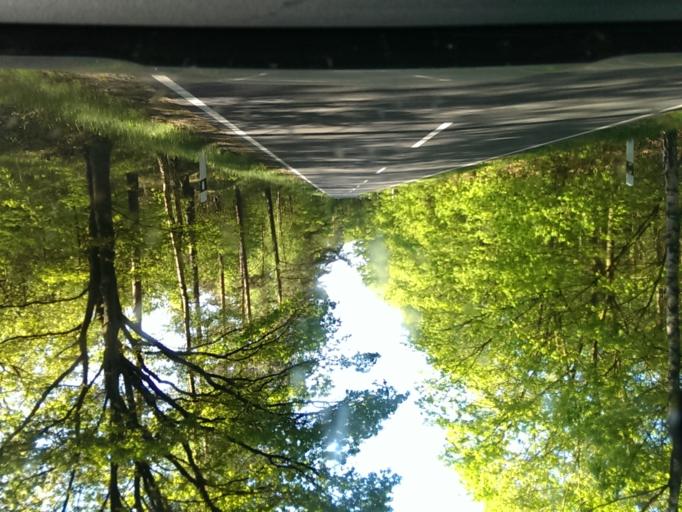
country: DE
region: Lower Saxony
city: Hambuhren
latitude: 52.6202
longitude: 9.9295
